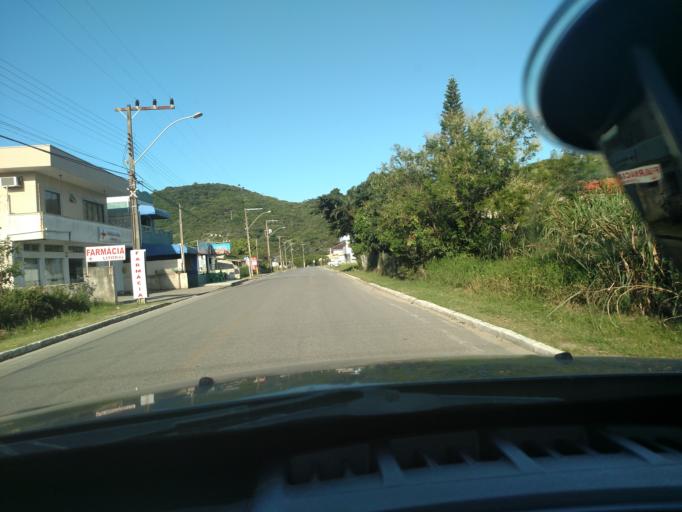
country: BR
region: Santa Catarina
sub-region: Porto Belo
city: Porto Belo
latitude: -27.1784
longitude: -48.5260
